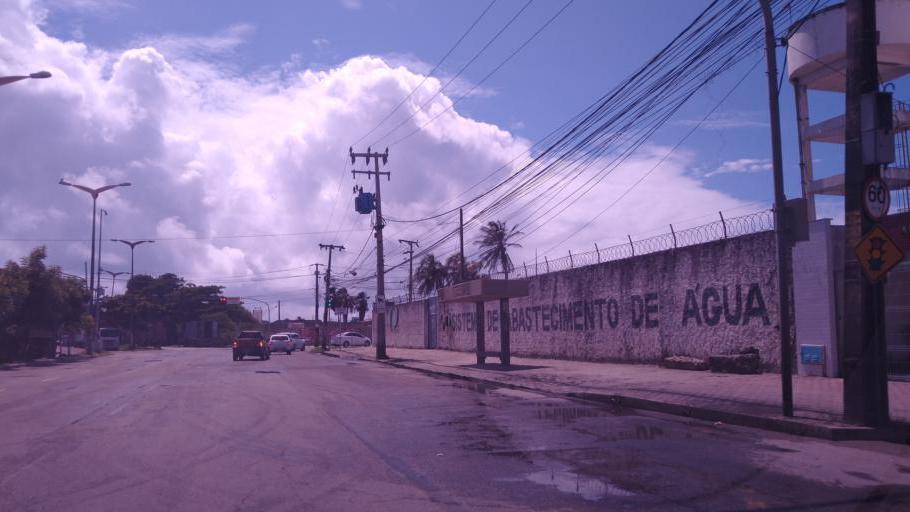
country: BR
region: Ceara
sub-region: Fortaleza
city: Fortaleza
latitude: -3.7144
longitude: -38.4735
